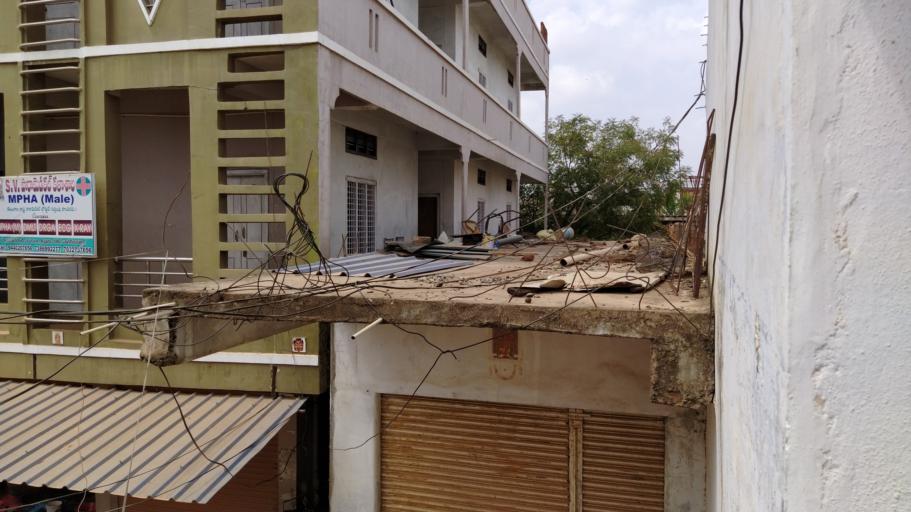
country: IN
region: Telangana
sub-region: Mahbubnagar
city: Nagar Karnul
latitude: 16.4832
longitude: 78.3114
